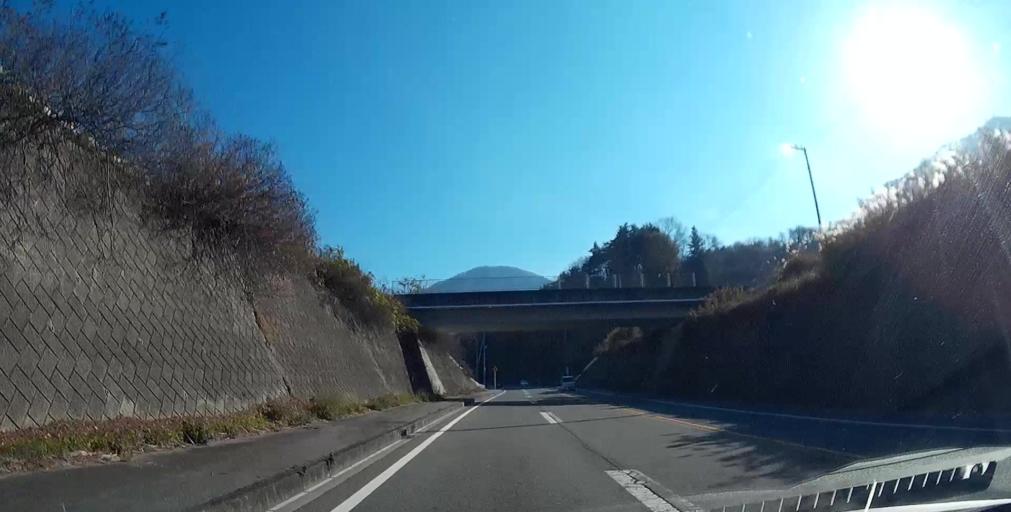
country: JP
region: Yamanashi
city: Isawa
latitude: 35.6009
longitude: 138.7080
